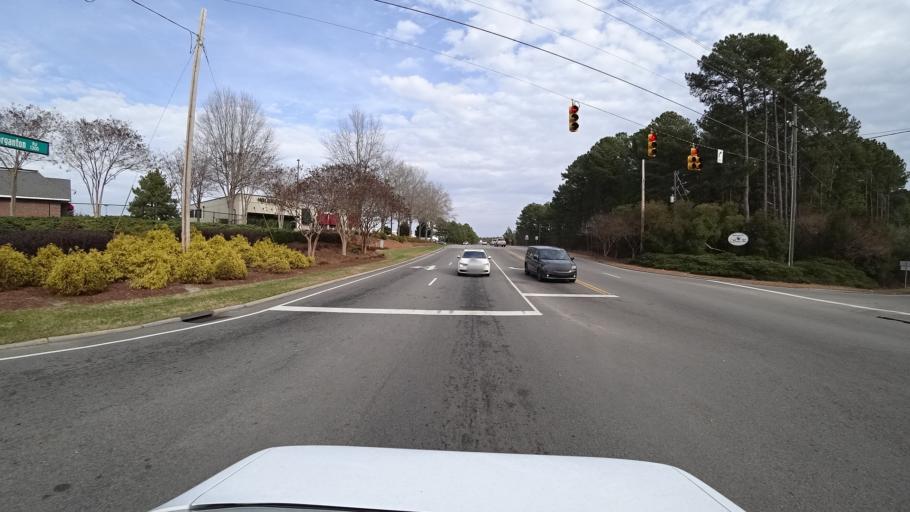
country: US
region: North Carolina
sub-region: Moore County
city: Southern Pines
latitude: 35.1775
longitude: -79.4315
